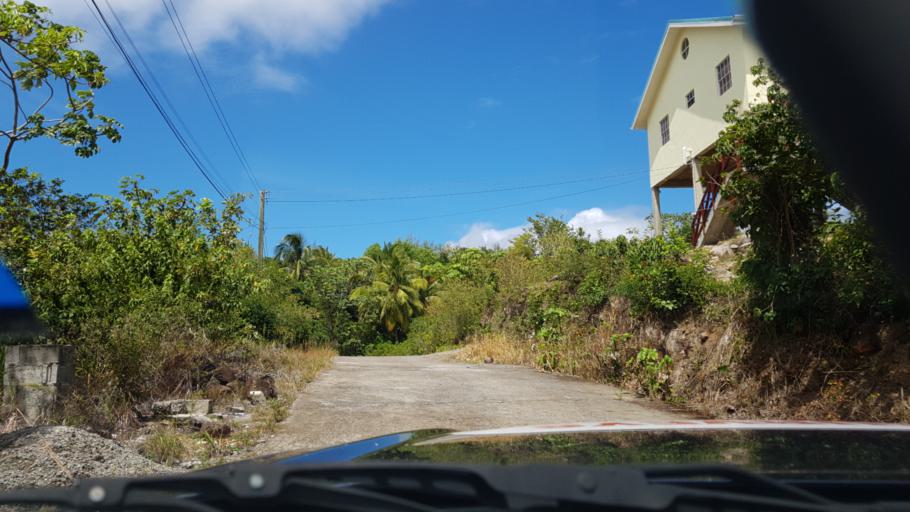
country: LC
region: Anse-la-Raye
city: Anse La Raye
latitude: 13.9441
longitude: -61.0350
